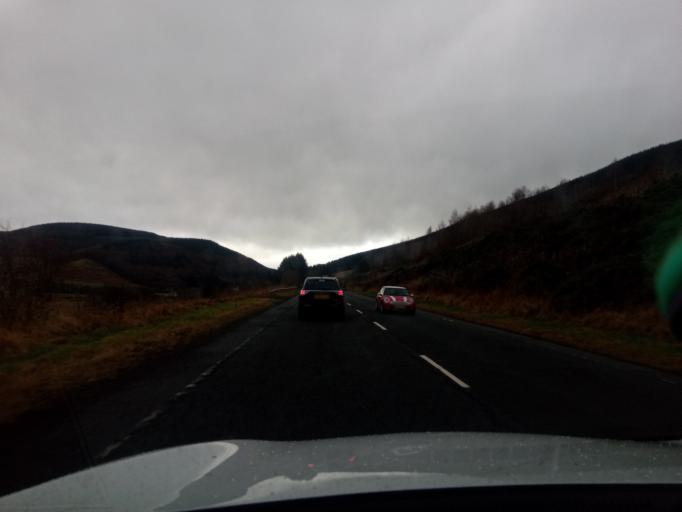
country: GB
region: Scotland
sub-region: The Scottish Borders
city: Innerleithen
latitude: 55.6289
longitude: -2.9974
